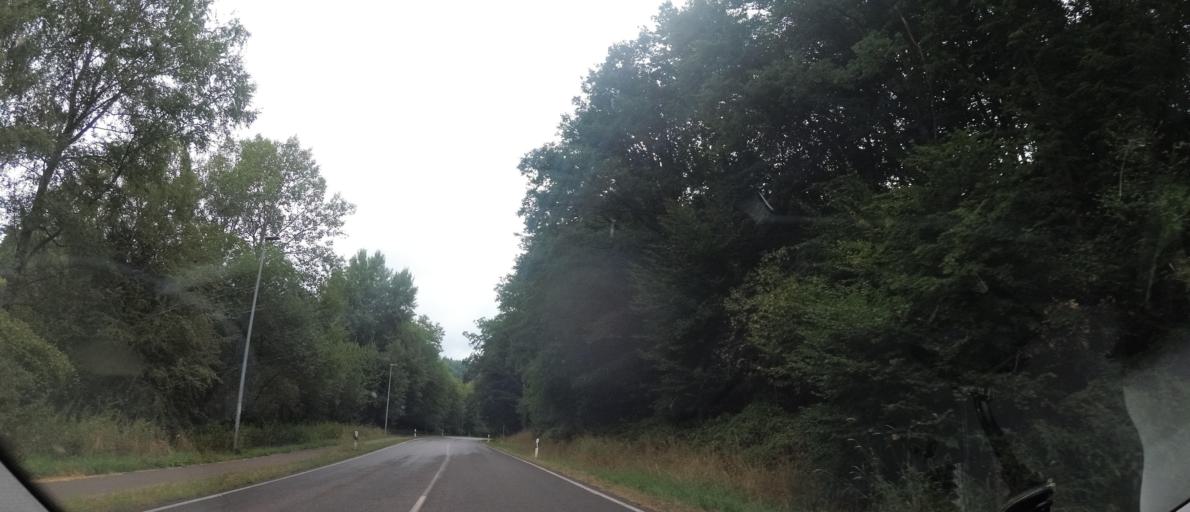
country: DE
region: Saarland
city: Sankt Ingbert
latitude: 49.2467
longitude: 7.1579
